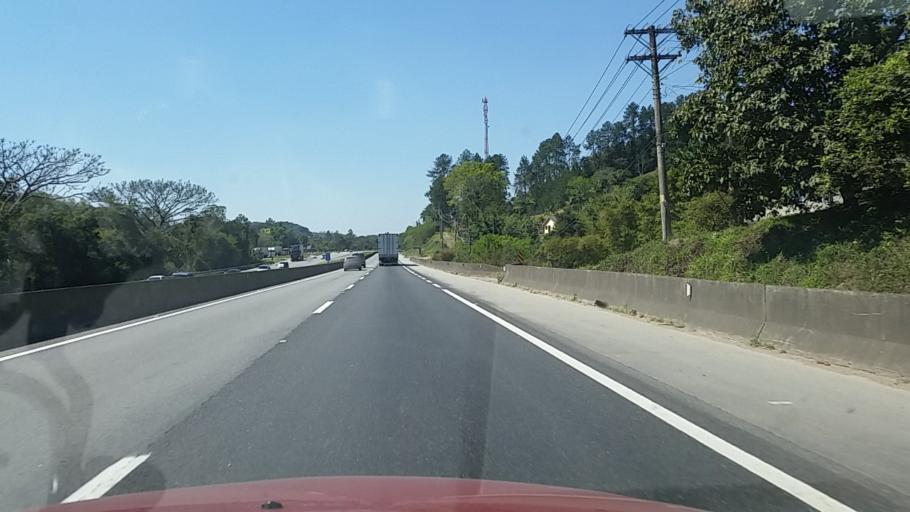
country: BR
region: Sao Paulo
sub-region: Juquitiba
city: Juquitiba
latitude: -23.9374
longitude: -47.0371
